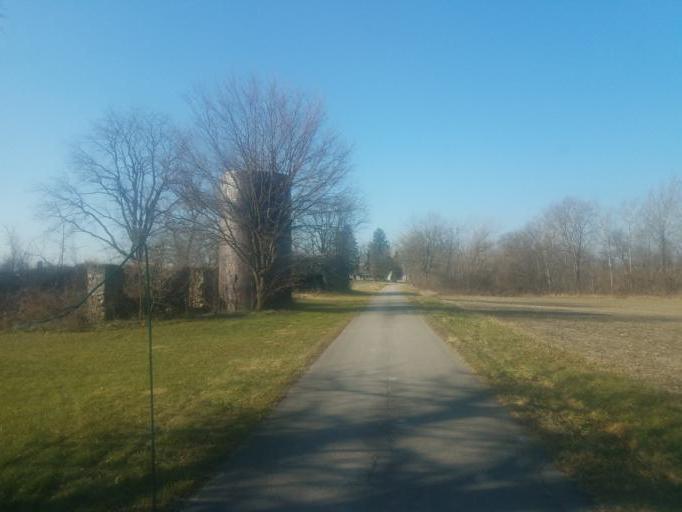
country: US
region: Ohio
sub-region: Seneca County
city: Tiffin
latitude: 41.0622
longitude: -83.0226
